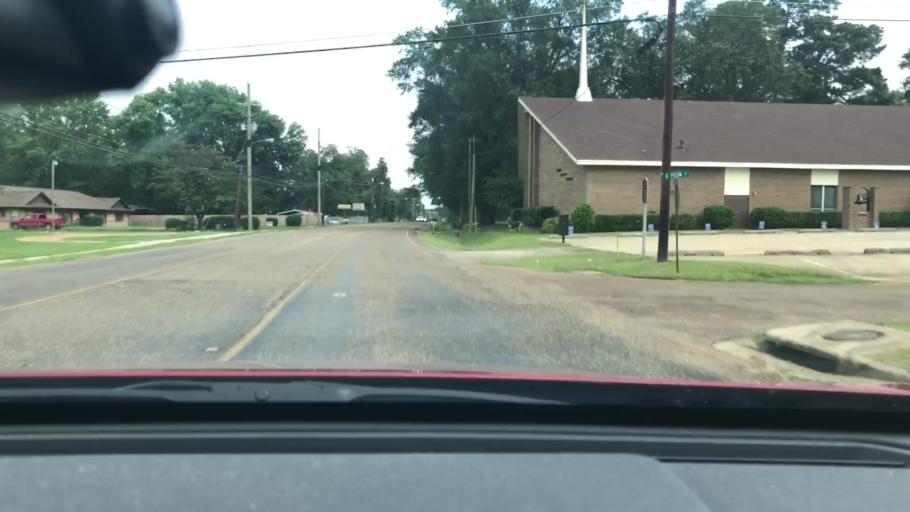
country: US
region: Texas
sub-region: Bowie County
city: Nash
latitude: 33.4427
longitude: -94.1229
